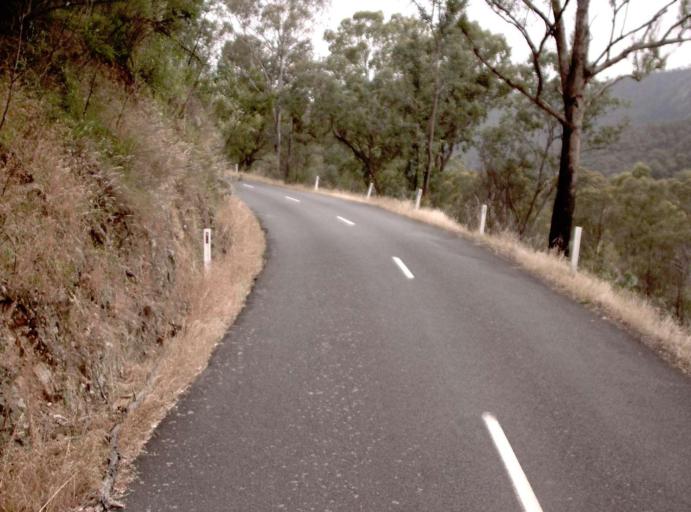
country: AU
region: Victoria
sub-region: Wellington
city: Heyfield
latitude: -37.7433
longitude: 146.6669
